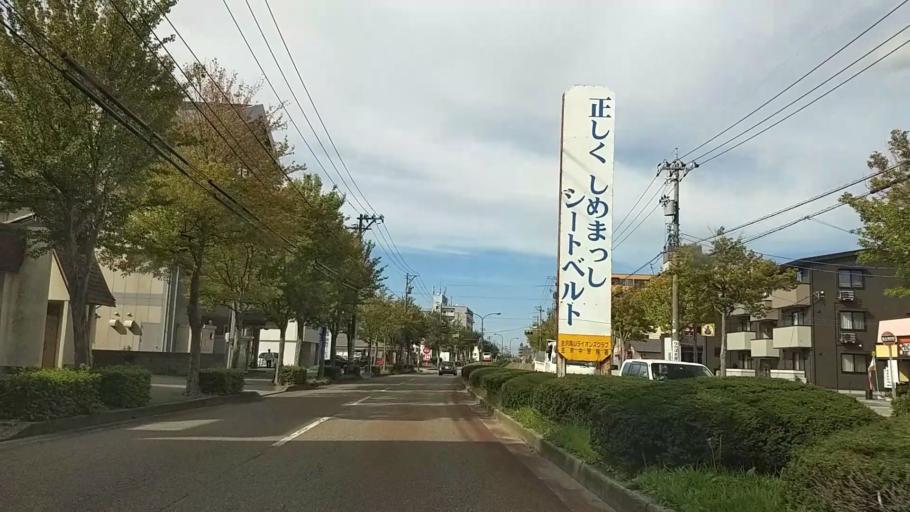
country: JP
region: Ishikawa
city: Nonoichi
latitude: 36.5300
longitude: 136.6381
